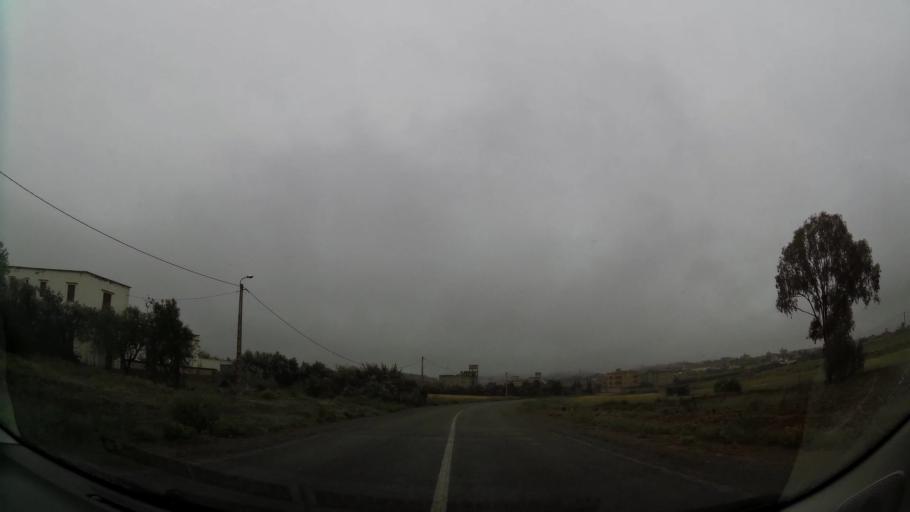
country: MA
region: Oriental
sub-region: Nador
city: Boudinar
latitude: 35.1130
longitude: -3.5752
